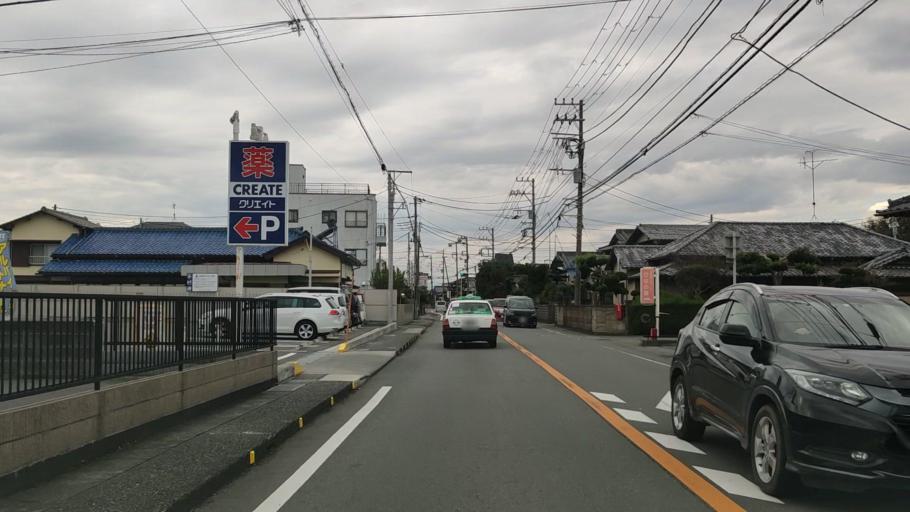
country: JP
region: Shizuoka
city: Numazu
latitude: 35.1108
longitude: 138.8307
